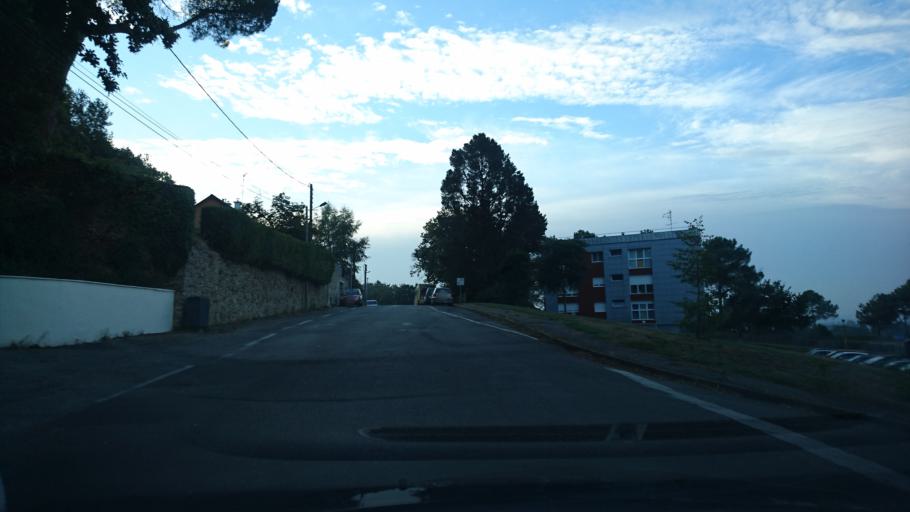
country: FR
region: Brittany
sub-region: Departement d'Ille-et-Vilaine
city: Redon
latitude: 47.6579
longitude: -2.0965
